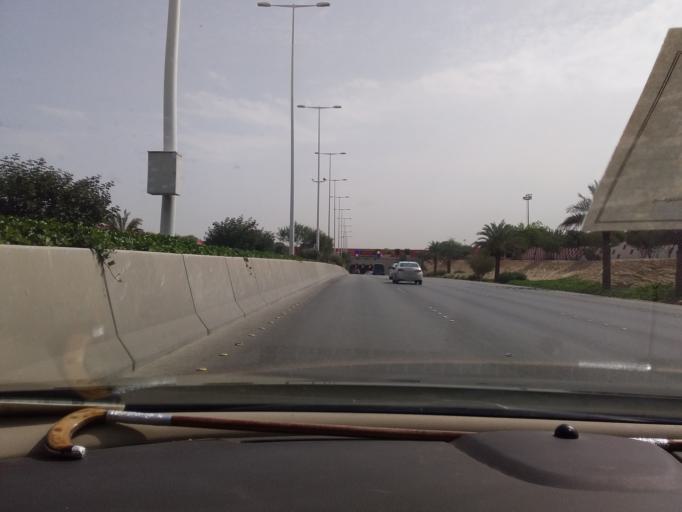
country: SA
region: Ar Riyad
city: Riyadh
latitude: 24.7133
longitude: 46.7183
